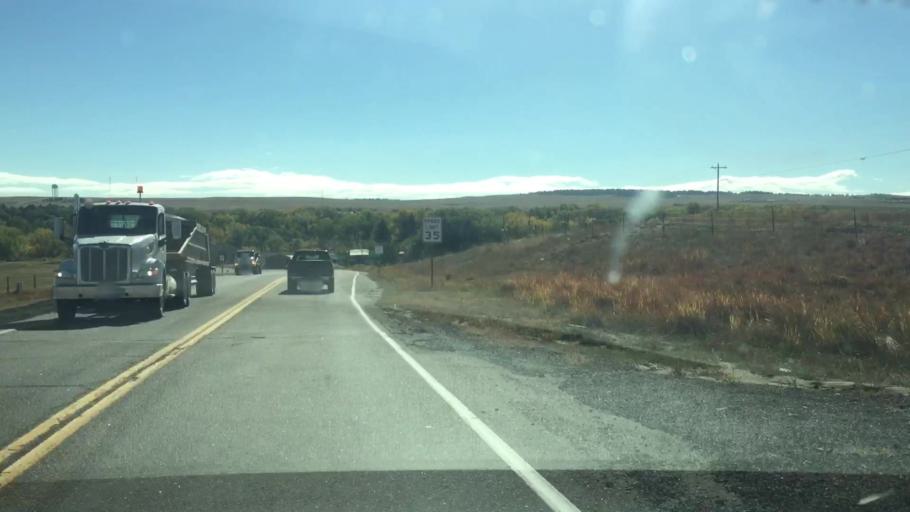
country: US
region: Colorado
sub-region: Elbert County
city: Kiowa
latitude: 39.3476
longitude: -104.4765
